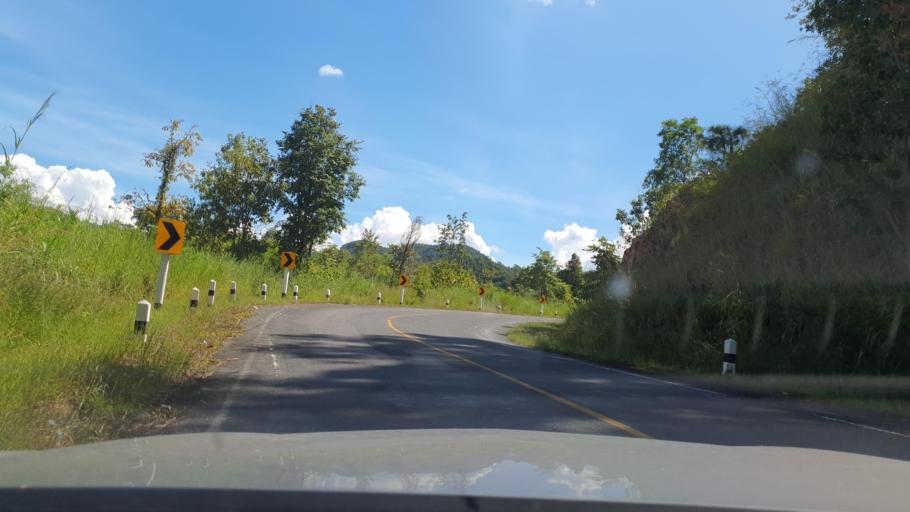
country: TH
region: Chiang Mai
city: Phrao
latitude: 19.3612
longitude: 99.2750
